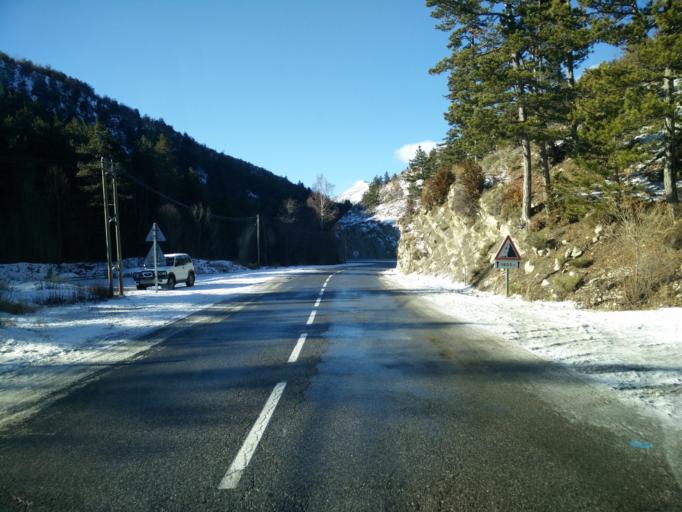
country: FR
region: Provence-Alpes-Cote d'Azur
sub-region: Departement des Alpes-de-Haute-Provence
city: Castellane
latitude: 43.9151
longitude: 6.5640
